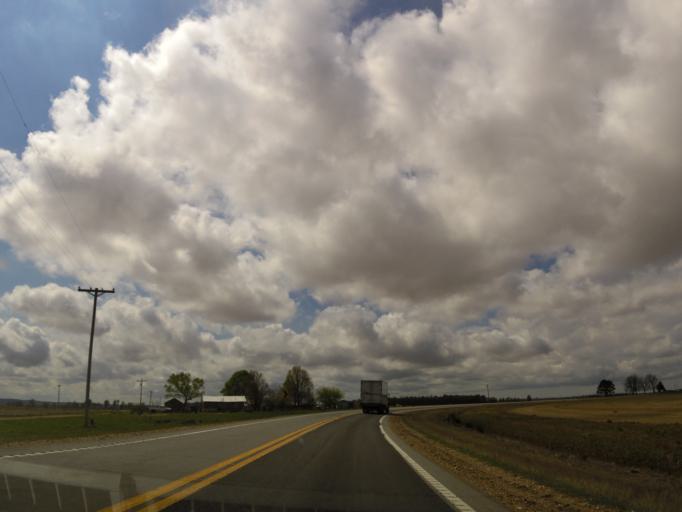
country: US
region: Arkansas
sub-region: Clay County
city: Corning
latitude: 36.3007
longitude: -90.5254
